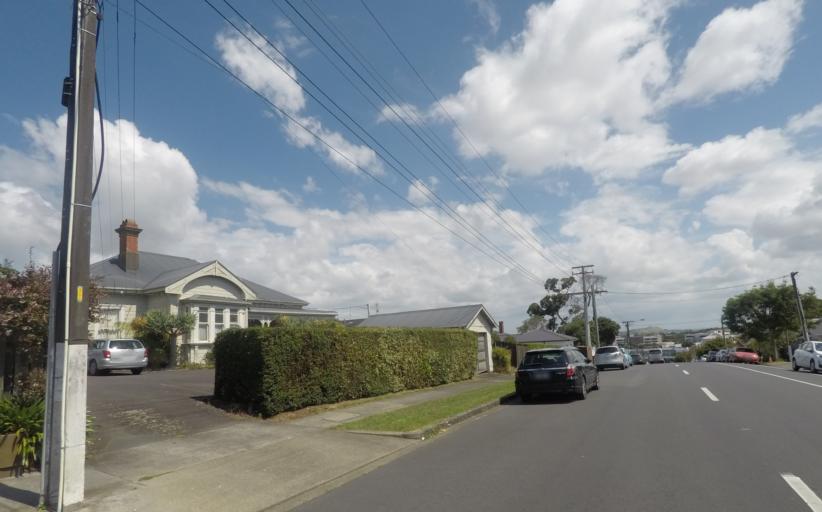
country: NZ
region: Auckland
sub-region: Auckland
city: Tamaki
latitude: -36.8955
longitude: 174.8103
